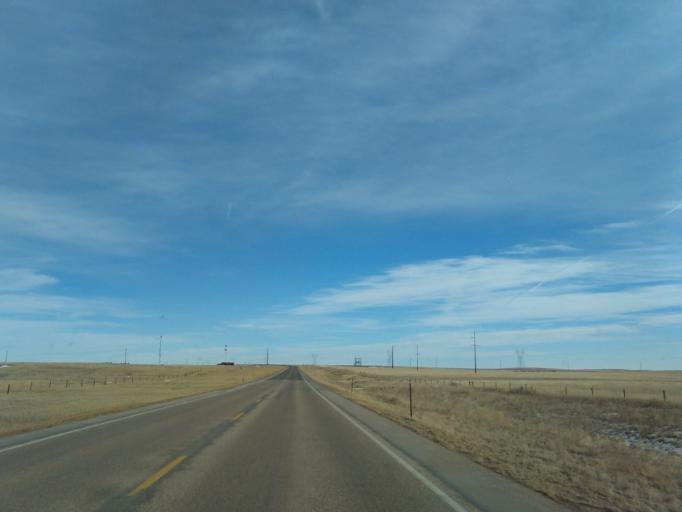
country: US
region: Wyoming
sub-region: Laramie County
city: Pine Bluffs
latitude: 41.4354
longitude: -104.3602
